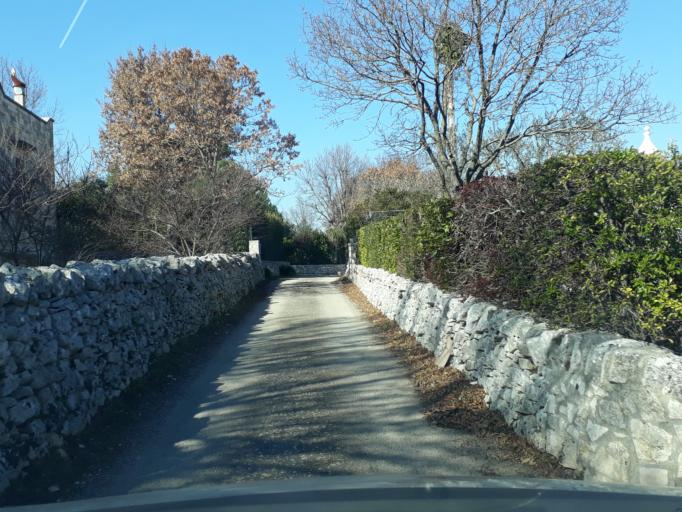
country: IT
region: Apulia
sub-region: Provincia di Brindisi
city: Lamie di Olimpie-Selva
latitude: 40.7980
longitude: 17.3463
